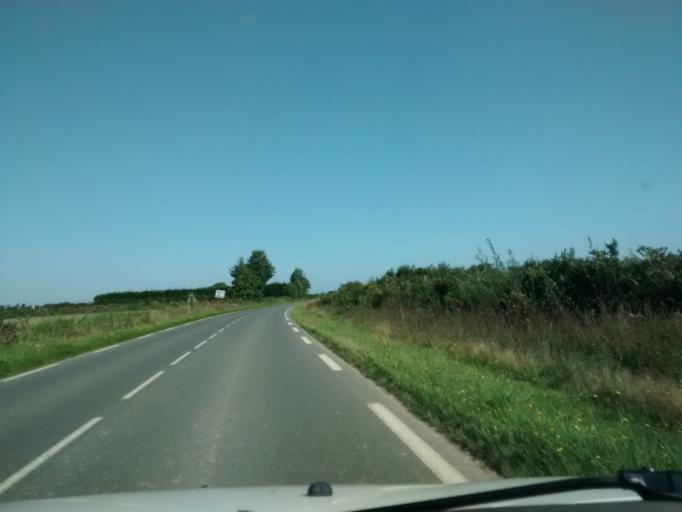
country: FR
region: Brittany
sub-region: Departement des Cotes-d'Armor
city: Tredarzec
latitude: 48.7953
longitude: -3.2014
